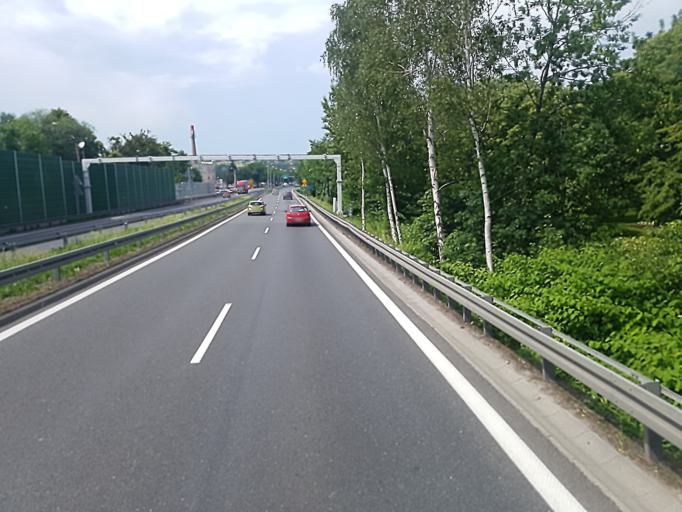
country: PL
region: Silesian Voivodeship
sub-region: Powiat cieszynski
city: Skoczow
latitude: 49.7992
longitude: 18.7927
